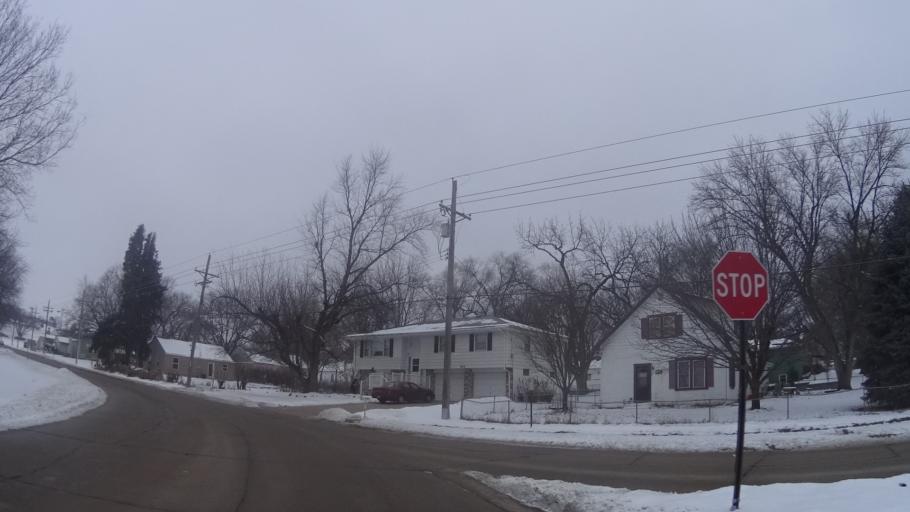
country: US
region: Nebraska
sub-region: Sarpy County
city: Bellevue
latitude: 41.1344
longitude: -95.9044
